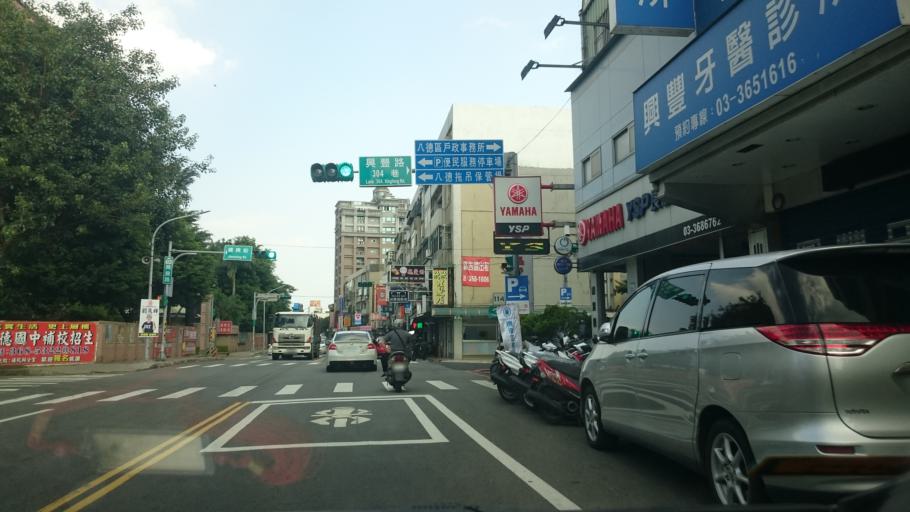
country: TW
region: Taiwan
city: Daxi
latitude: 24.9293
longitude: 121.2861
